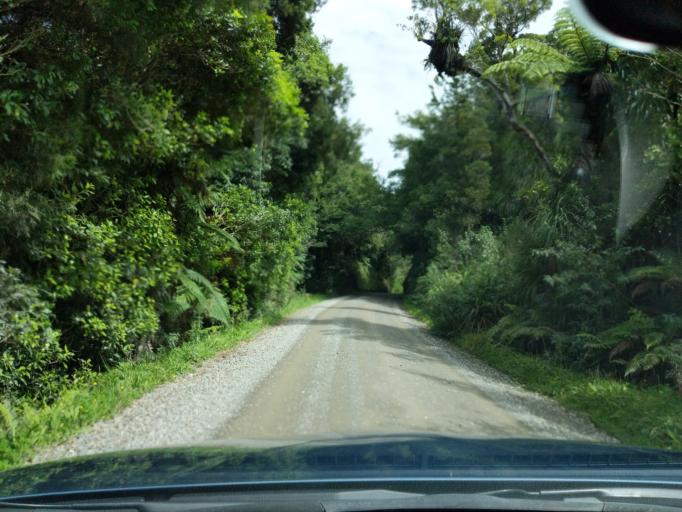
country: NZ
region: Tasman
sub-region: Tasman District
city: Takaka
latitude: -40.6454
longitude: 172.4758
